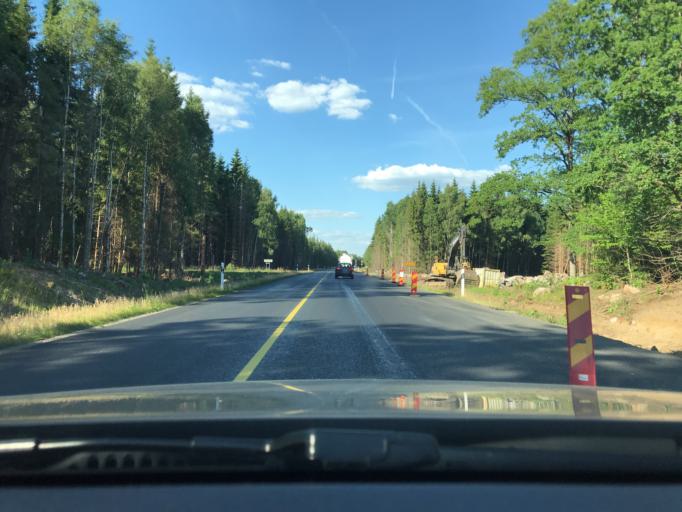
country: SE
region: Kronoberg
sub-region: Almhults Kommun
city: AElmhult
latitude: 56.6378
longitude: 14.2642
